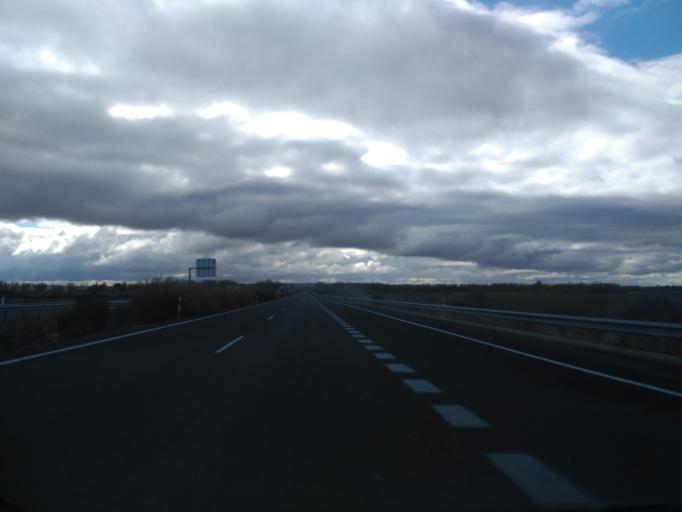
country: ES
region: Castille and Leon
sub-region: Provincia de Palencia
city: Fromista
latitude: 42.2609
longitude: -4.4174
